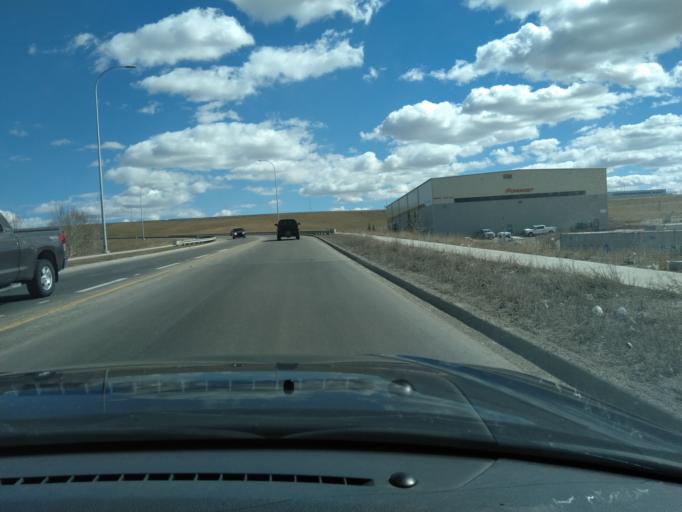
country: CA
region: Alberta
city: Calgary
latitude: 51.1105
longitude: -114.0332
